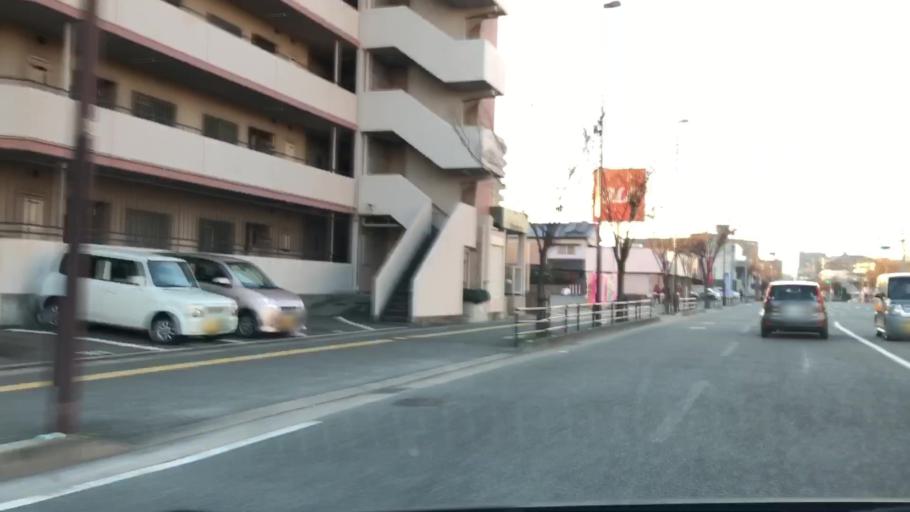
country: JP
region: Fukuoka
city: Fukuoka-shi
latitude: 33.6186
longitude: 130.4346
